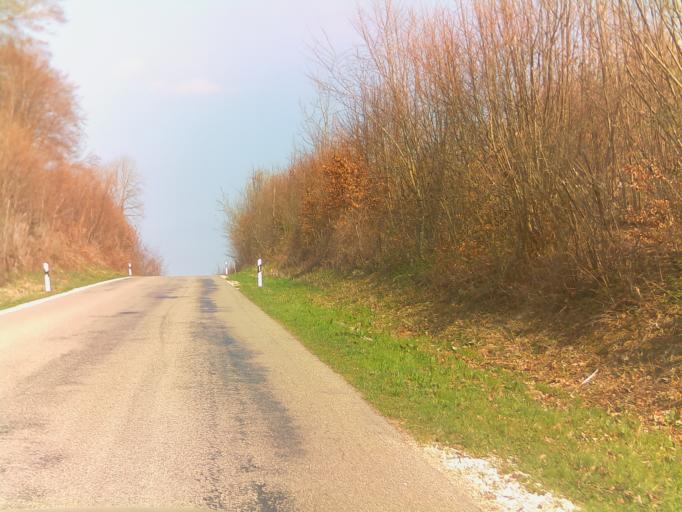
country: DE
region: Bavaria
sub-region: Swabia
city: Altenstadt
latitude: 48.1685
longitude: 10.1342
